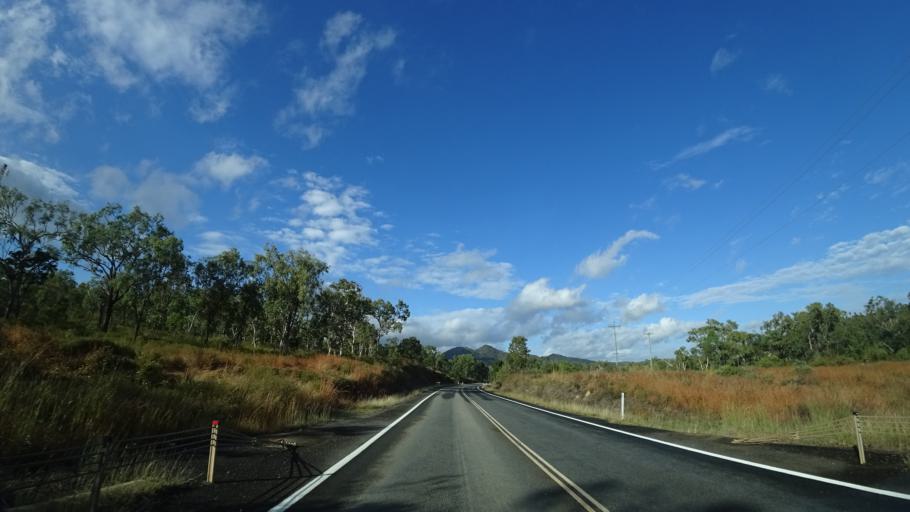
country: AU
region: Queensland
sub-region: Cook
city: Cooktown
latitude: -15.6149
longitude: 145.2210
